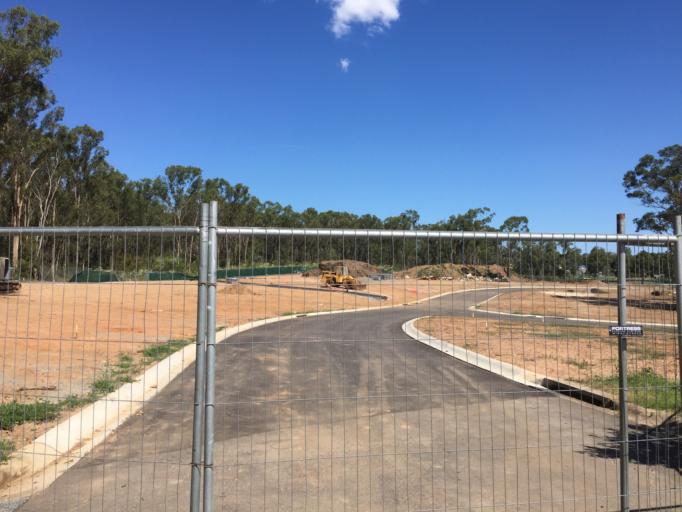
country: AU
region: New South Wales
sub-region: Blacktown
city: Blacktown
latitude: -33.7899
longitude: 150.8945
